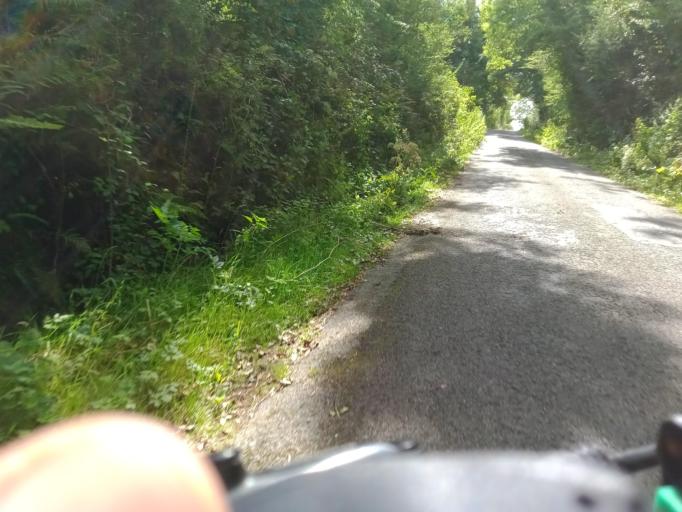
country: IE
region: Munster
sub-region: Waterford
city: Dungarvan
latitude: 52.1394
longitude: -7.5059
